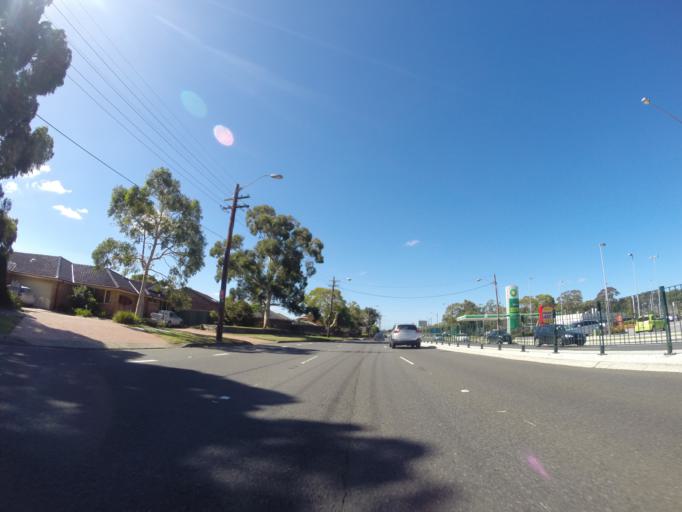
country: AU
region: New South Wales
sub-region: Sutherland Shire
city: Heathcote
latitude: -34.0782
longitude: 151.0106
